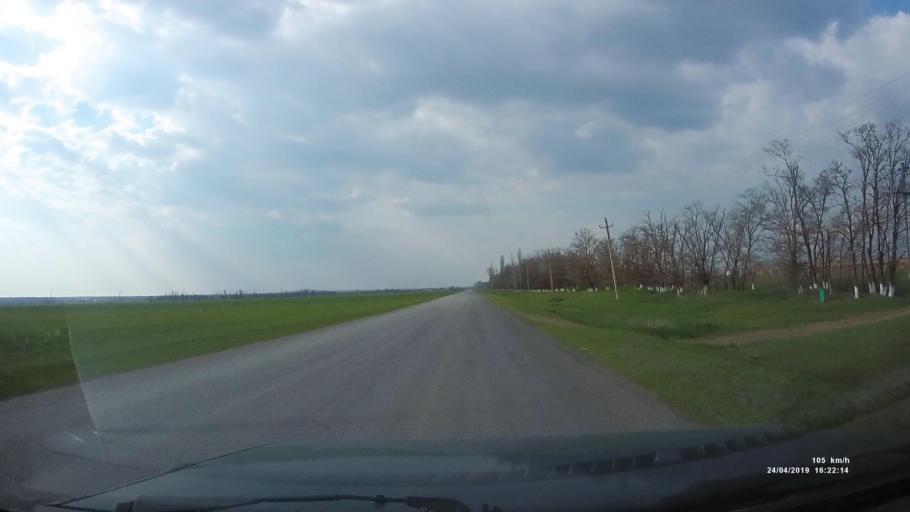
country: RU
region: Rostov
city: Orlovskiy
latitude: 46.8167
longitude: 42.0581
